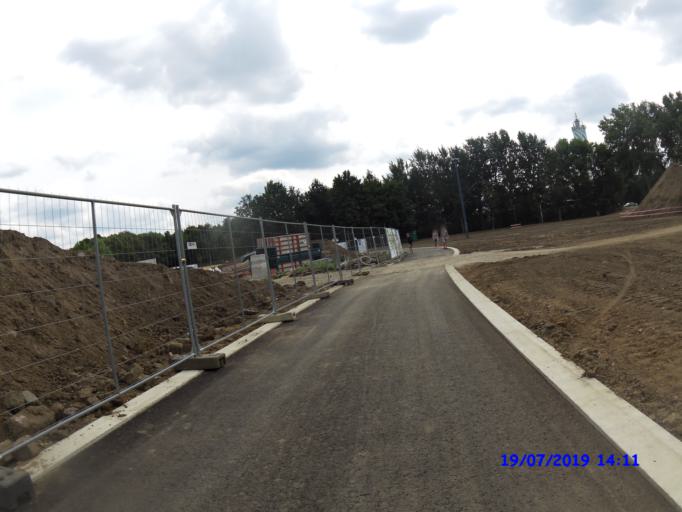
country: BE
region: Flanders
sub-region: Provincie Limburg
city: Hasselt
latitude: 50.9349
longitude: 5.3523
